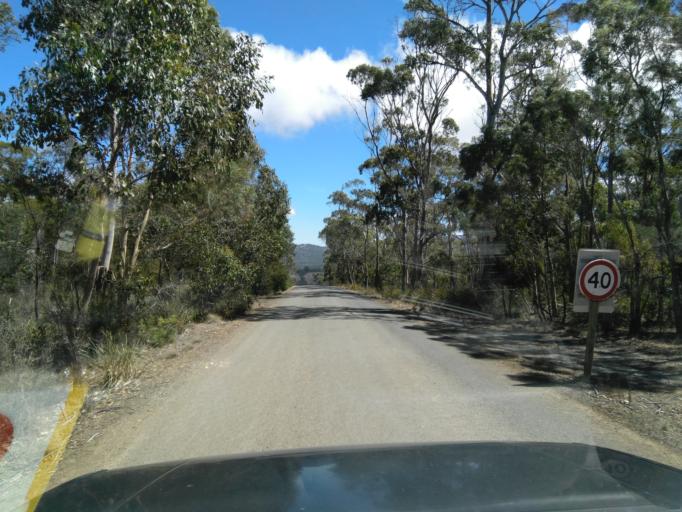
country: AU
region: Tasmania
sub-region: Kingborough
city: Taroona
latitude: -42.9495
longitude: 147.3270
